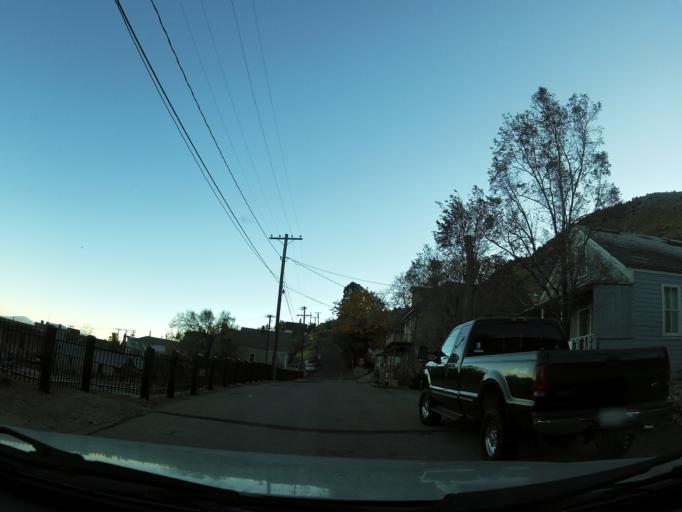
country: US
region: Nevada
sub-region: Storey County
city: Virginia City
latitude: 39.3106
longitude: -119.6510
